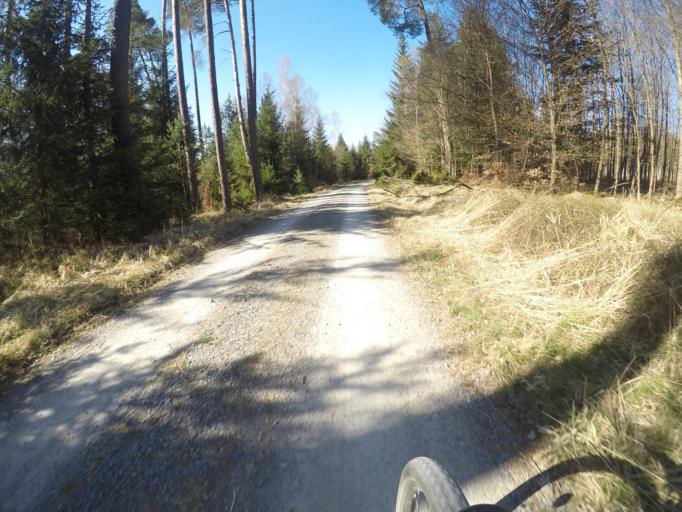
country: DE
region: Baden-Wuerttemberg
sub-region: Regierungsbezirk Stuttgart
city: Weil im Schonbuch
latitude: 48.5928
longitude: 9.0507
